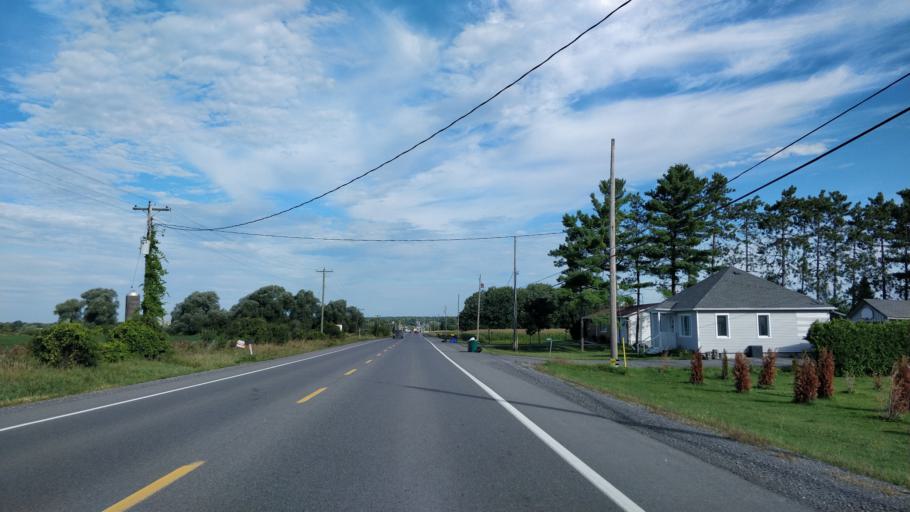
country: CA
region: Ontario
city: Bells Corners
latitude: 45.3296
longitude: -76.0171
